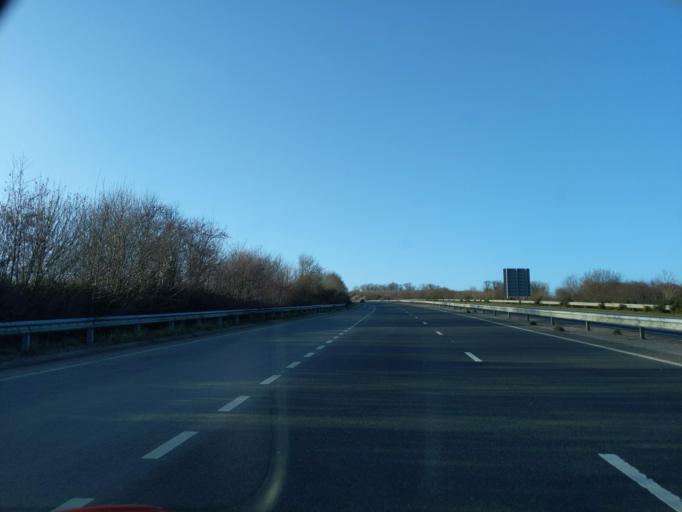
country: GB
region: England
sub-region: Cornwall
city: Liskeard
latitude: 50.4587
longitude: -4.5087
